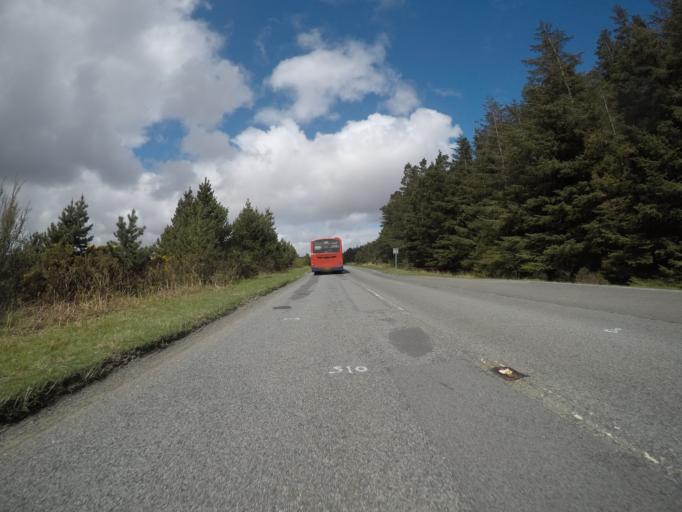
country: GB
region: Scotland
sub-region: Highland
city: Isle of Skye
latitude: 57.3154
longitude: -6.2003
